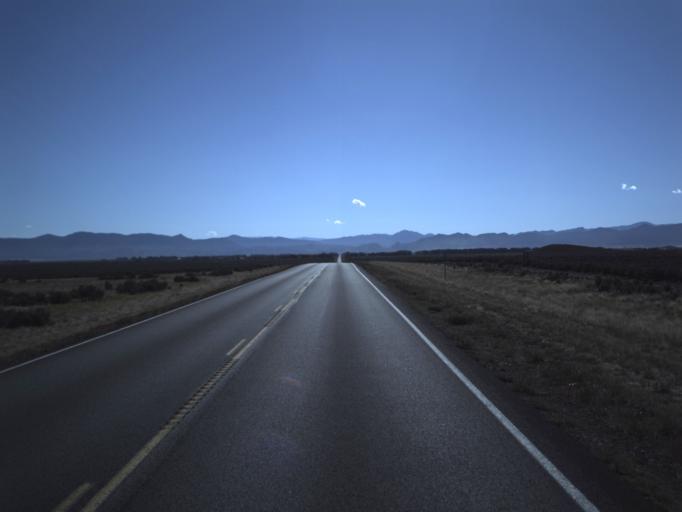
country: US
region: Utah
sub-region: Washington County
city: Enterprise
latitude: 37.7342
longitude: -113.7252
